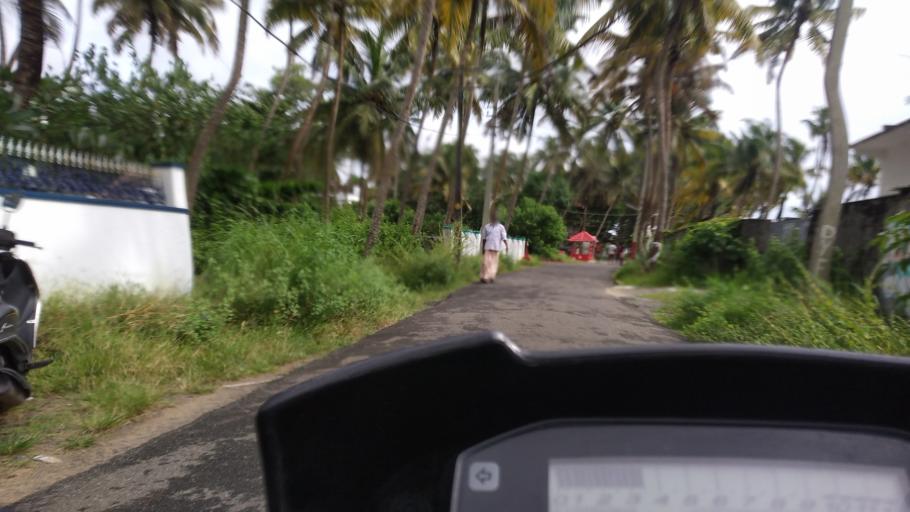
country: IN
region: Kerala
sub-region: Thrissur District
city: Kodungallur
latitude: 10.1602
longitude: 76.1720
